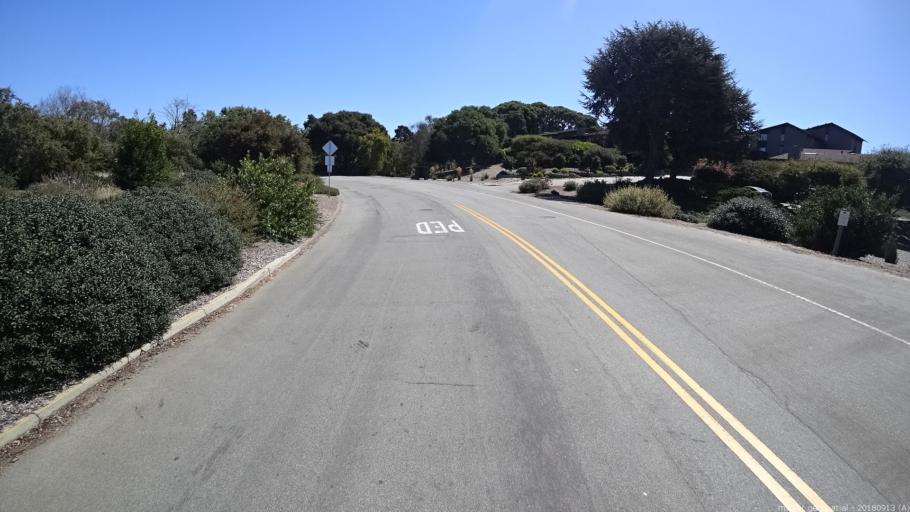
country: US
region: California
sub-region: Monterey County
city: Carmel-by-the-Sea
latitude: 36.5336
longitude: -121.8699
